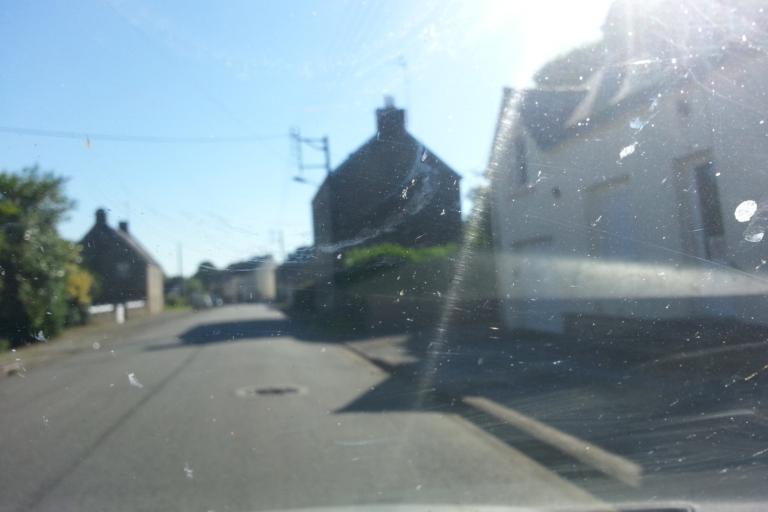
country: FR
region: Brittany
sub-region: Departement du Morbihan
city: Priziac
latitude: 48.0561
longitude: -3.4153
